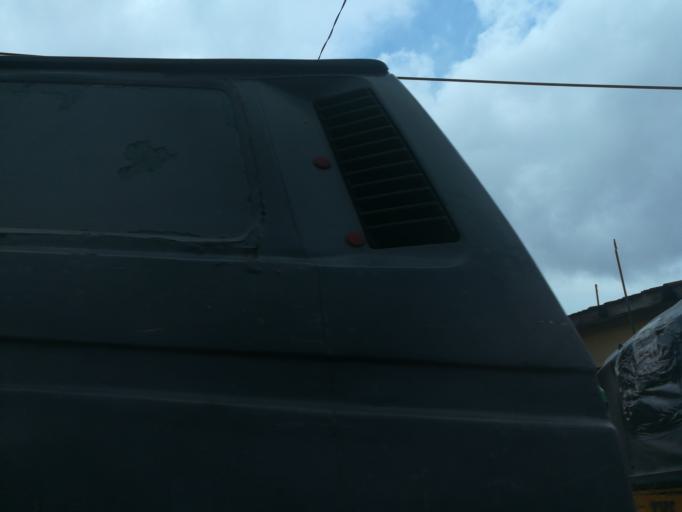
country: NG
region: Lagos
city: Agege
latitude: 6.6104
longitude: 3.3275
